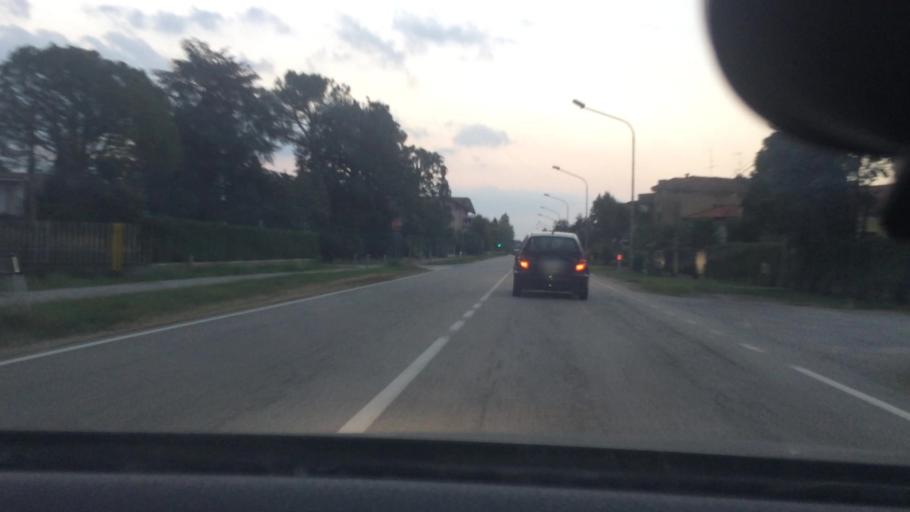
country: IT
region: Lombardy
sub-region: Citta metropolitana di Milano
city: Buscate
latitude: 45.5439
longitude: 8.8040
